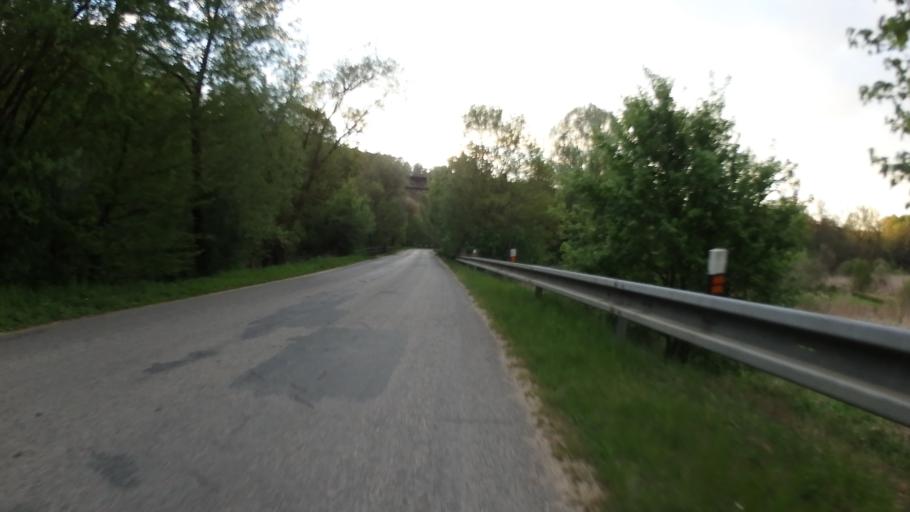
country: CZ
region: South Moravian
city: Strelice
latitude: 49.1461
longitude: 16.4671
